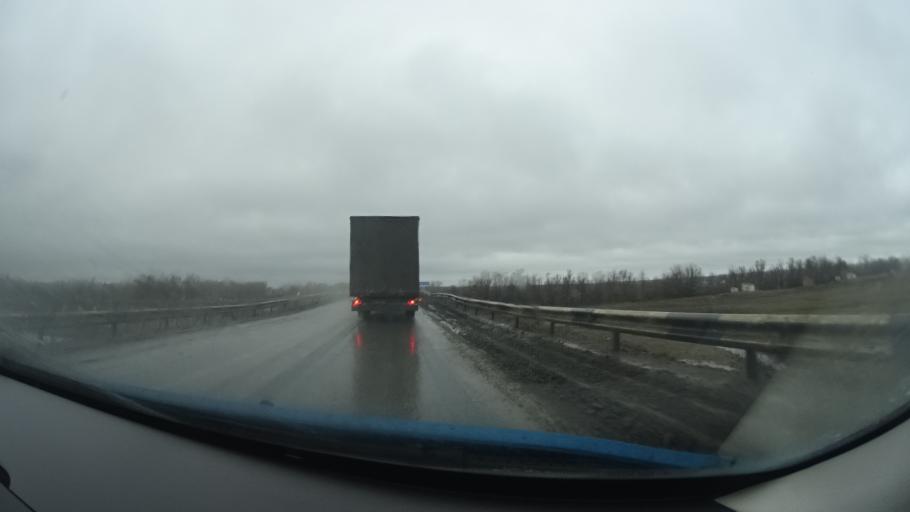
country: RU
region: Bashkortostan
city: Buzdyak
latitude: 54.6601
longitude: 54.6730
